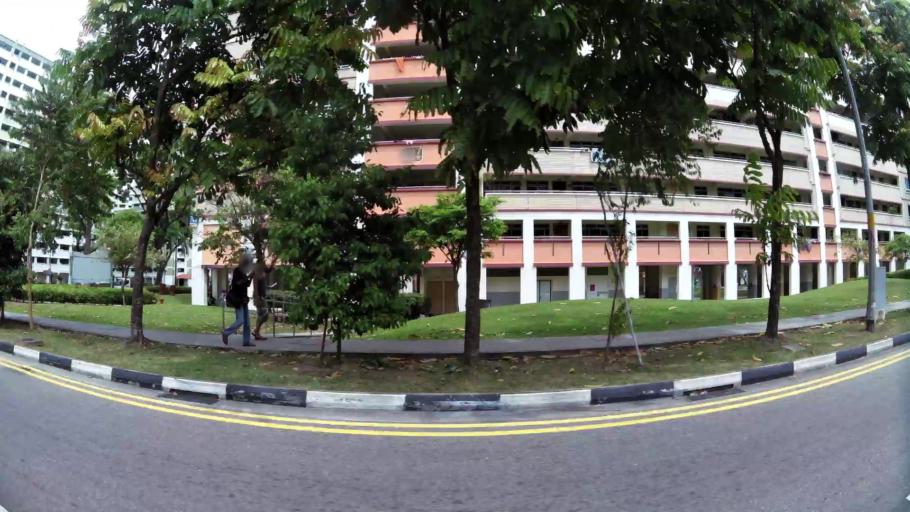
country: MY
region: Johor
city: Johor Bahru
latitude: 1.3417
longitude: 103.6937
